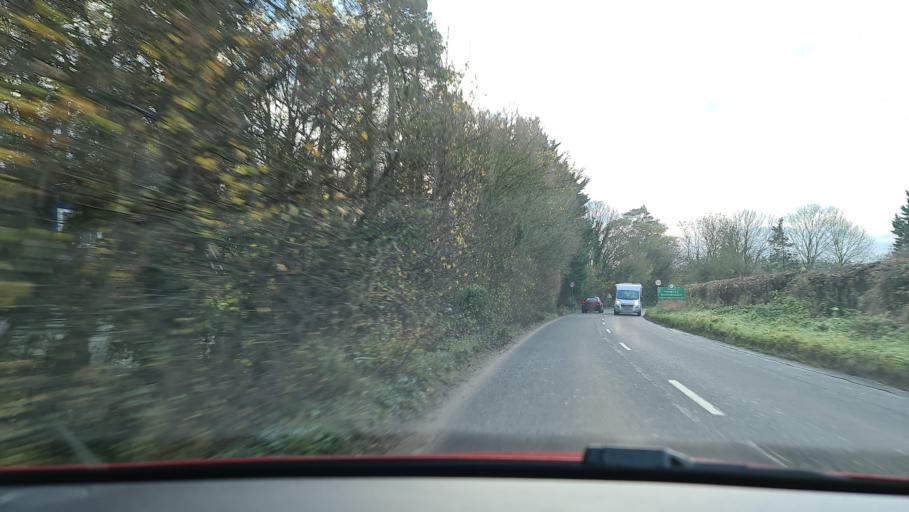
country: GB
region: England
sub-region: Buckinghamshire
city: Princes Risborough
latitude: 51.7260
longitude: -0.8493
